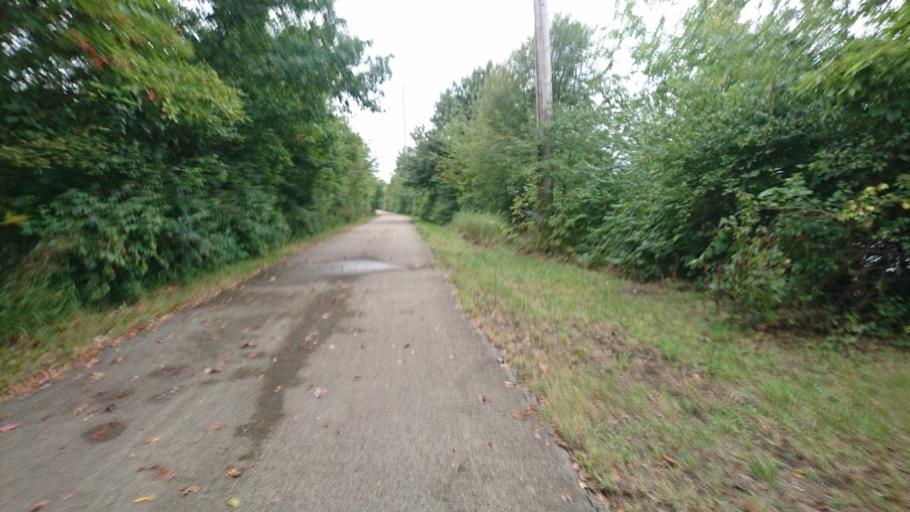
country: US
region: Illinois
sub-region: Sangamon County
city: Chatham
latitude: 39.7060
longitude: -89.6878
